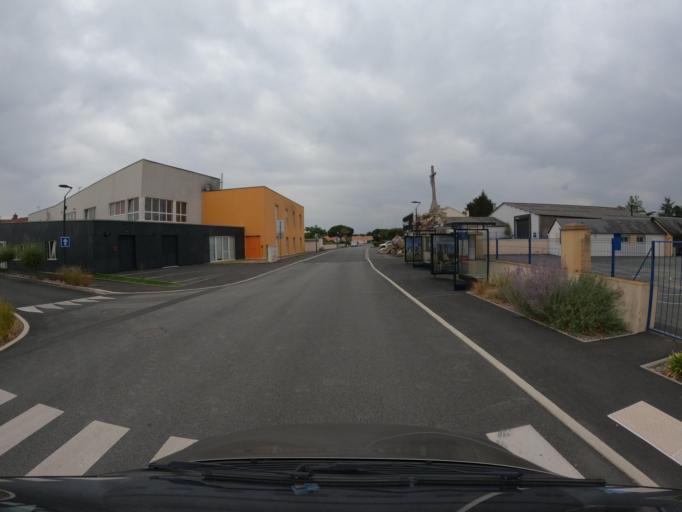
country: FR
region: Pays de la Loire
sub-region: Departement de la Vendee
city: La Guyonniere
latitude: 46.9670
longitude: -1.2503
